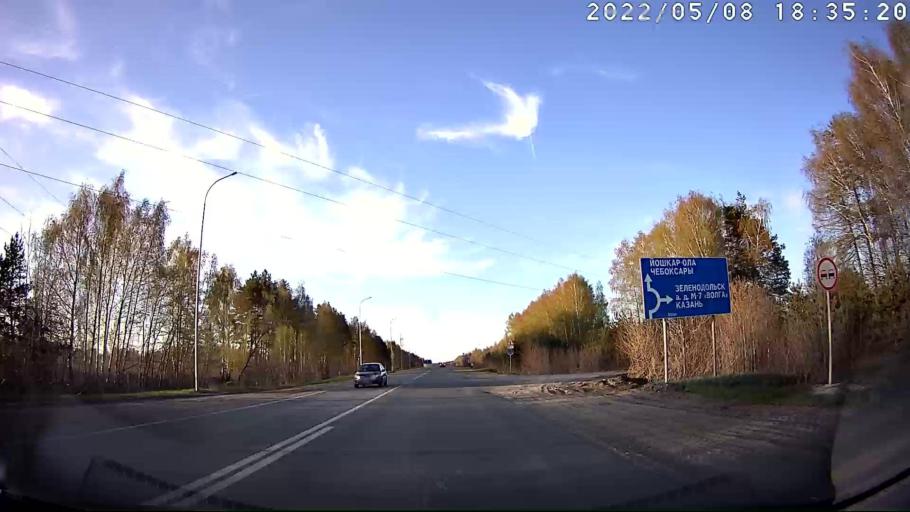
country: RU
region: Mariy-El
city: Volzhsk
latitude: 55.9083
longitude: 48.3617
